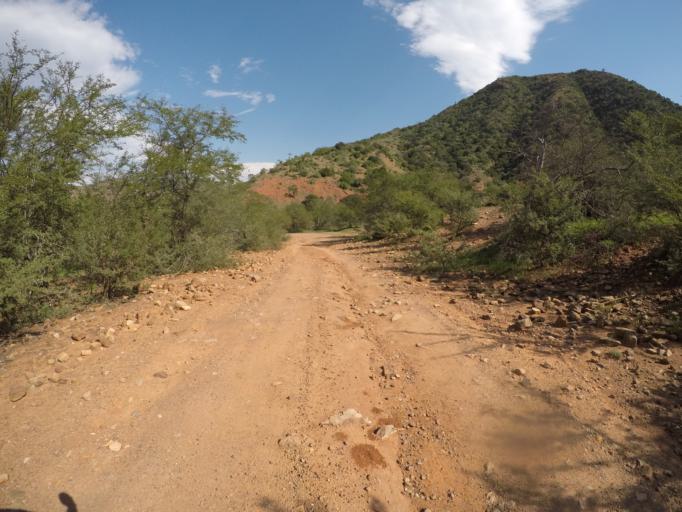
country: ZA
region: Eastern Cape
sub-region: Cacadu District Municipality
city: Kareedouw
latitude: -33.6596
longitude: 24.3972
